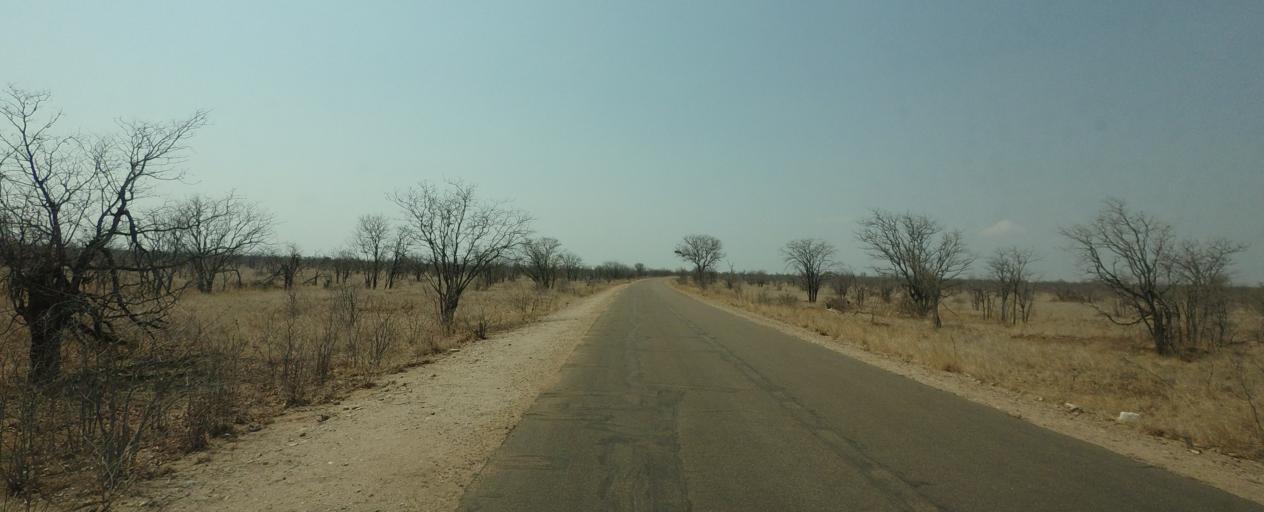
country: ZA
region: Limpopo
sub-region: Mopani District Municipality
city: Giyani
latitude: -23.3506
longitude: 31.3188
